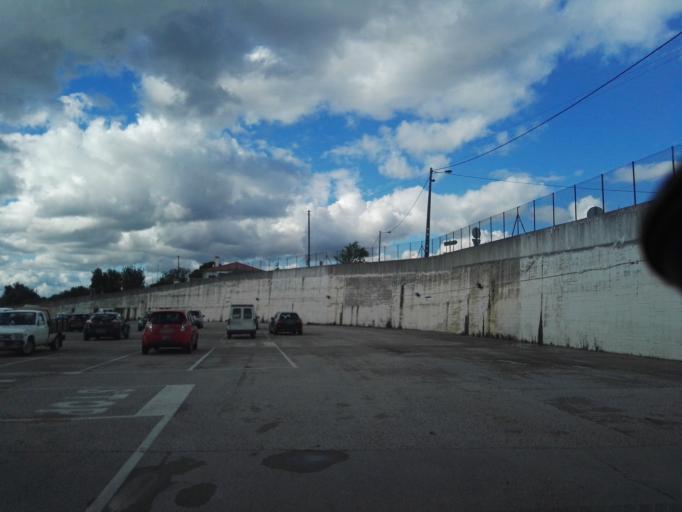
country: PT
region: Santarem
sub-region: Torres Novas
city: Torres Novas
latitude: 39.4676
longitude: -8.5242
